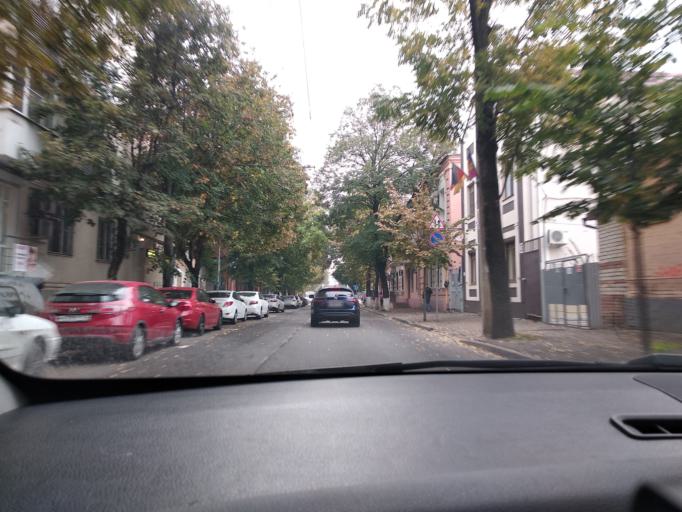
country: RU
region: Krasnodarskiy
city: Krasnodar
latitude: 45.0217
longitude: 38.9635
